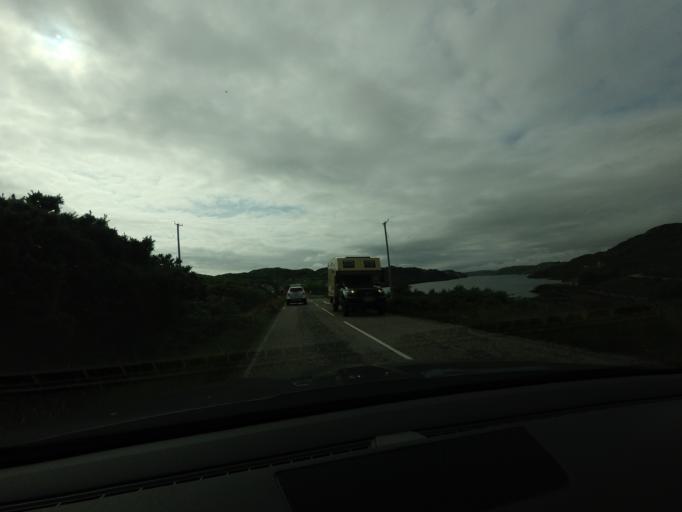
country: GB
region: Scotland
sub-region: Highland
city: Ullapool
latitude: 58.4246
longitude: -4.9868
